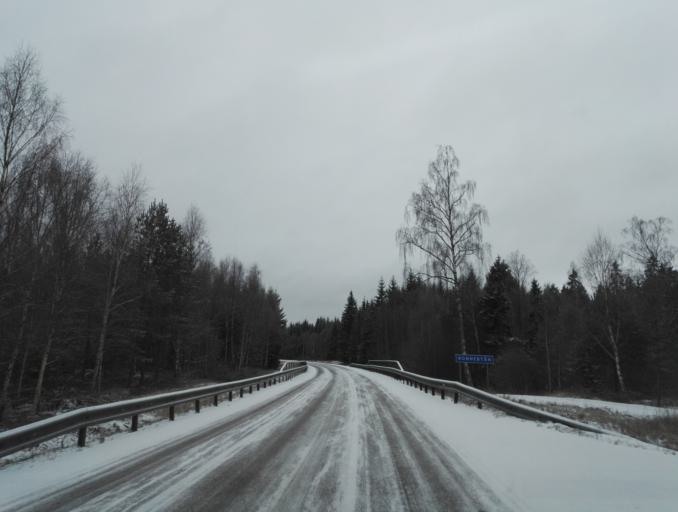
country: SE
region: Kronoberg
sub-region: Lessebo Kommun
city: Lessebo
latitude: 56.7287
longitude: 15.2023
